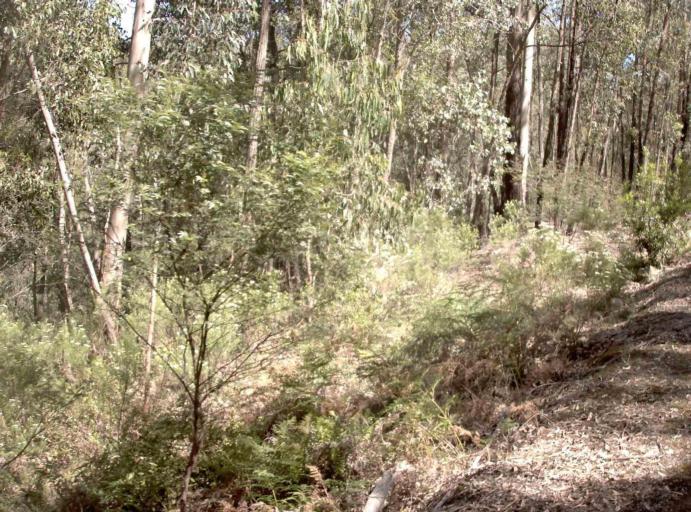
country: AU
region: Victoria
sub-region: East Gippsland
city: Lakes Entrance
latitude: -37.3825
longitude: 148.2188
